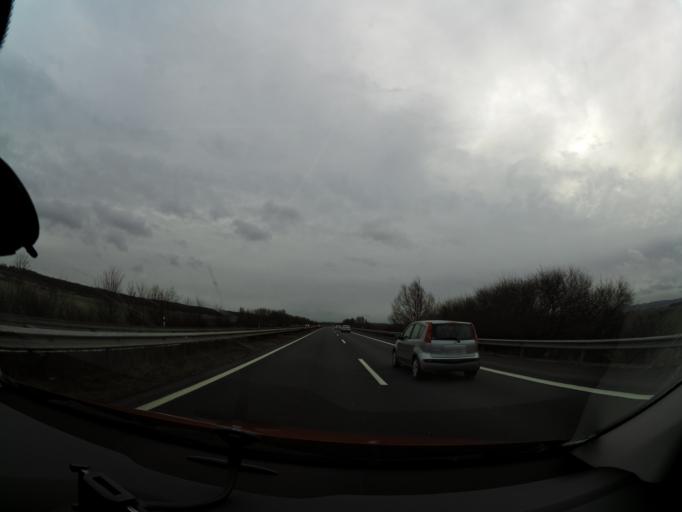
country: DE
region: Lower Saxony
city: Flothe
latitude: 52.0938
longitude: 10.4938
